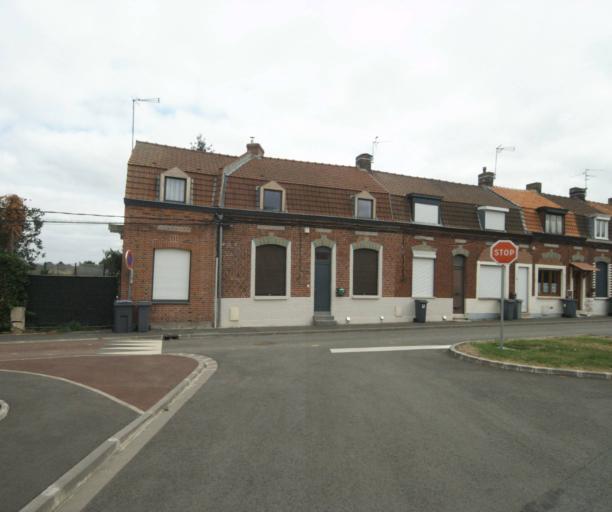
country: FR
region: Nord-Pas-de-Calais
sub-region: Departement du Nord
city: Toufflers
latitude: 50.6629
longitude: 3.2296
